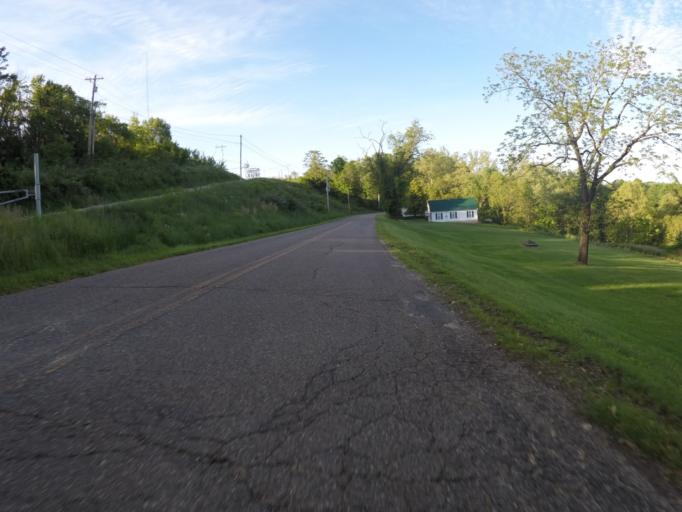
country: US
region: West Virginia
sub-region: Cabell County
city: Huntington
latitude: 38.5083
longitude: -82.4267
